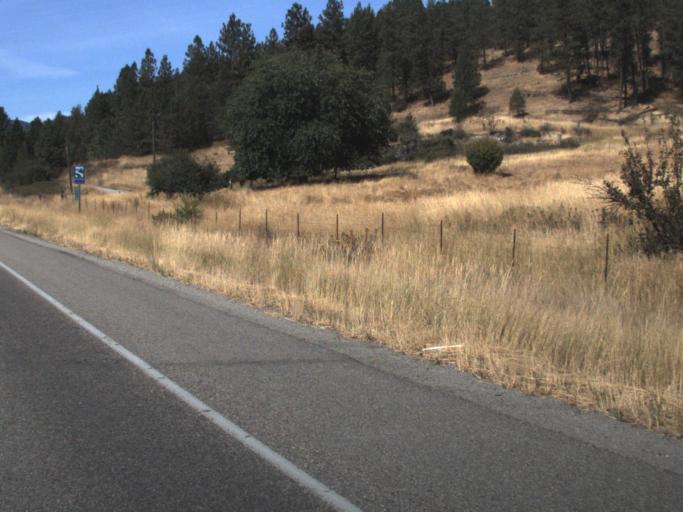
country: US
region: Washington
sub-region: Stevens County
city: Chewelah
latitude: 48.3124
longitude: -117.7970
